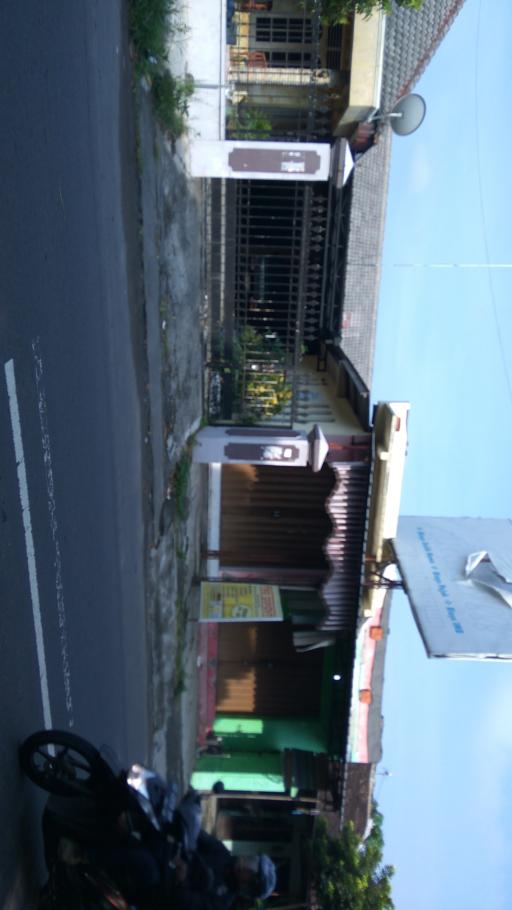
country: ID
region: Central Java
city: Ngemplak
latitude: -7.5362
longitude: 110.6812
